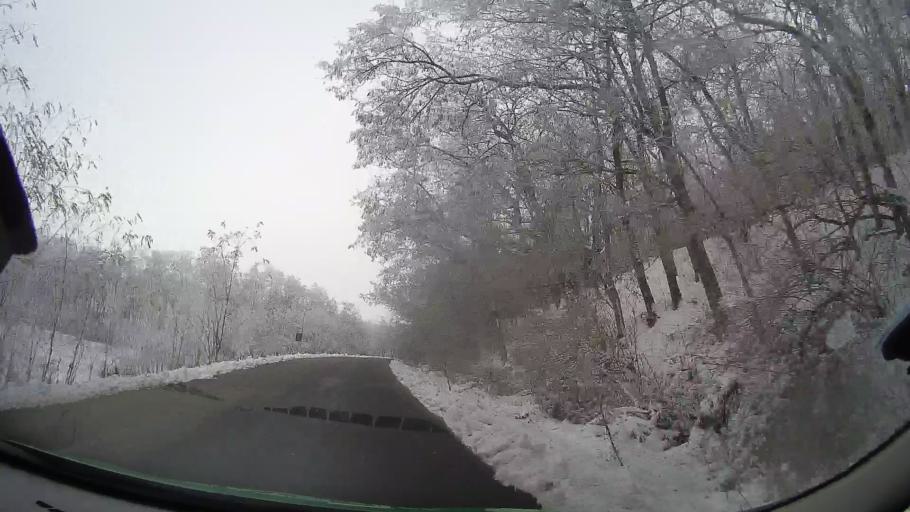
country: RO
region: Bacau
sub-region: Comuna Glavanesti
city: Frumuselu
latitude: 46.2647
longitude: 27.3252
